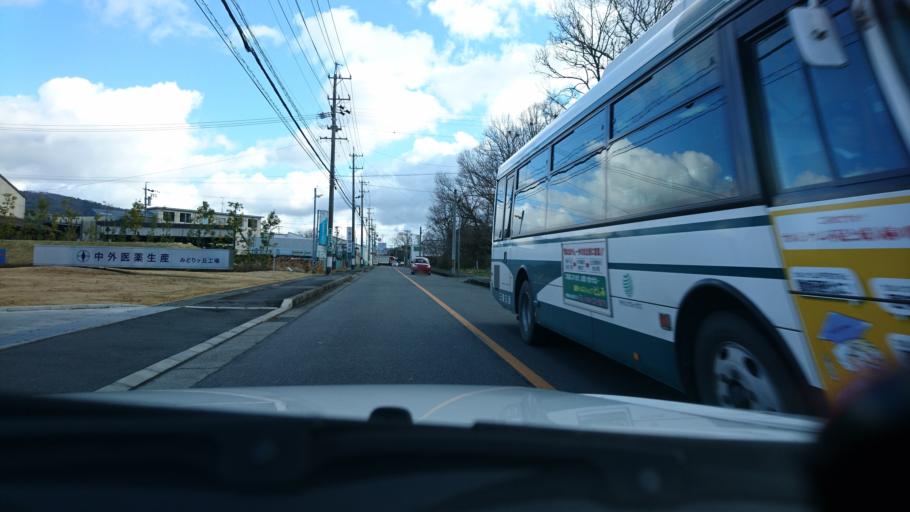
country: JP
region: Mie
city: Ueno-ebisumachi
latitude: 34.7600
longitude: 136.1550
